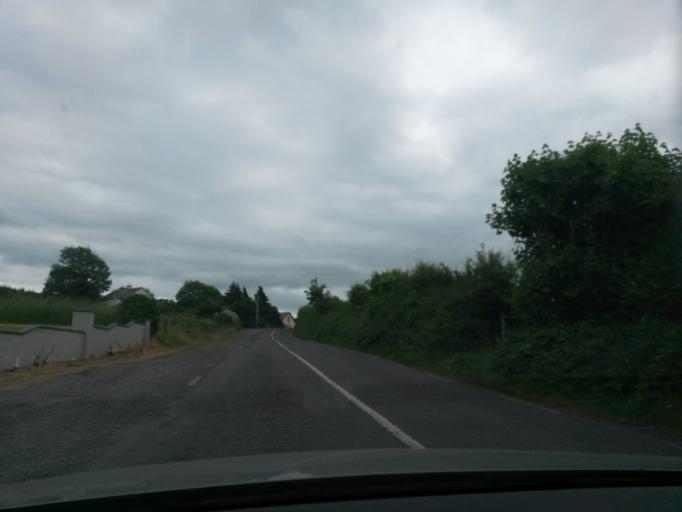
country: IE
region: Munster
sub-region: An Clar
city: Ennis
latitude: 52.9647
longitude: -9.0816
